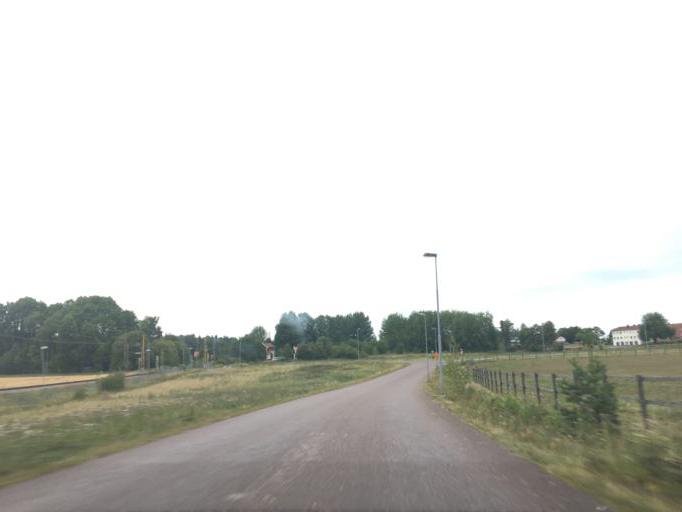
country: SE
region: Vaestmanland
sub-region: Hallstahammars Kommun
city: Kolback
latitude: 59.5257
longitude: 16.2431
